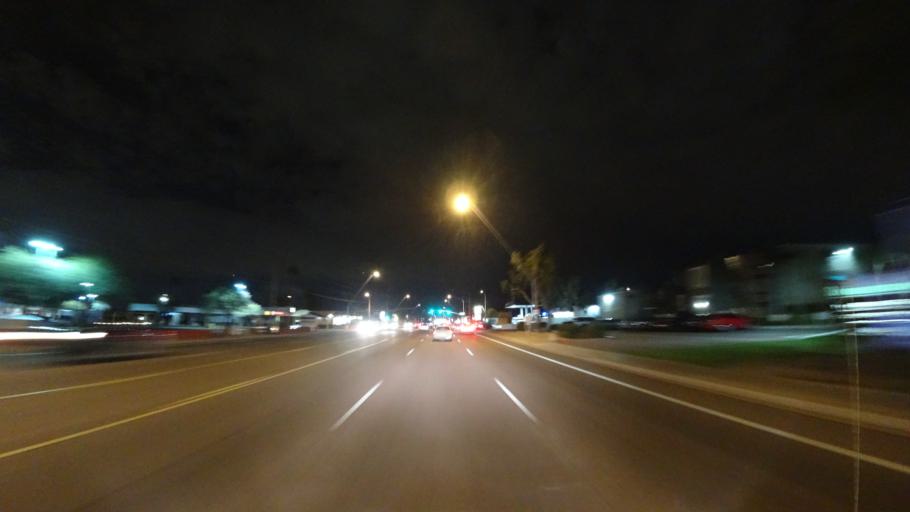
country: US
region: Arizona
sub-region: Maricopa County
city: Mesa
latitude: 33.3991
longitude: -111.8570
